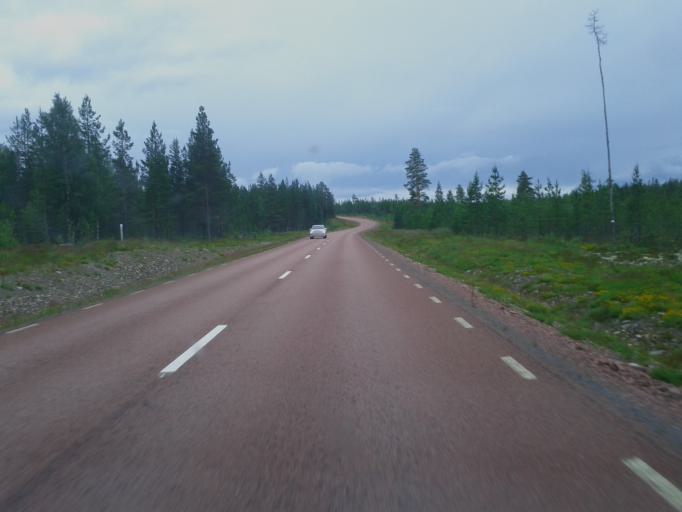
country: SE
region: Dalarna
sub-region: Alvdalens Kommun
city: AElvdalen
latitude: 61.6268
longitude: 13.2331
